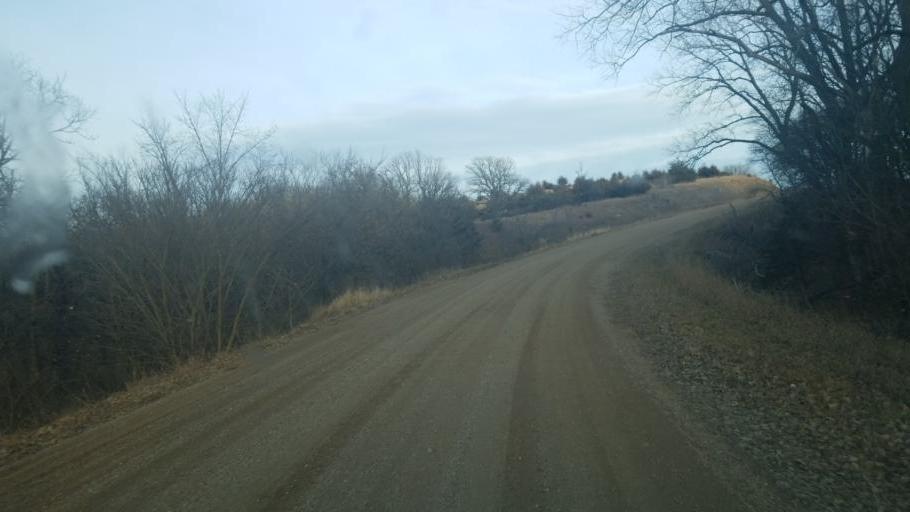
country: US
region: Nebraska
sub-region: Knox County
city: Center
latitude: 42.6918
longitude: -97.8025
